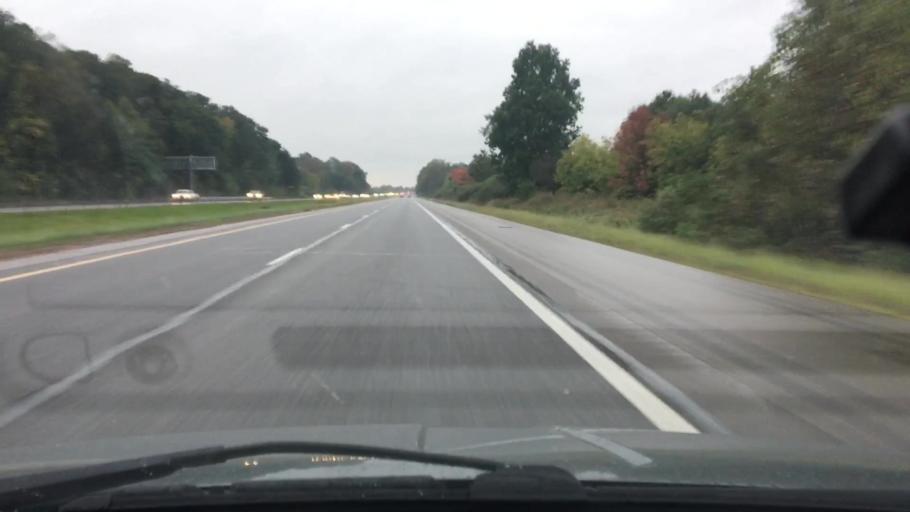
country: US
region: Michigan
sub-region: Washtenaw County
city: Dexter
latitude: 42.2974
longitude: -83.9112
